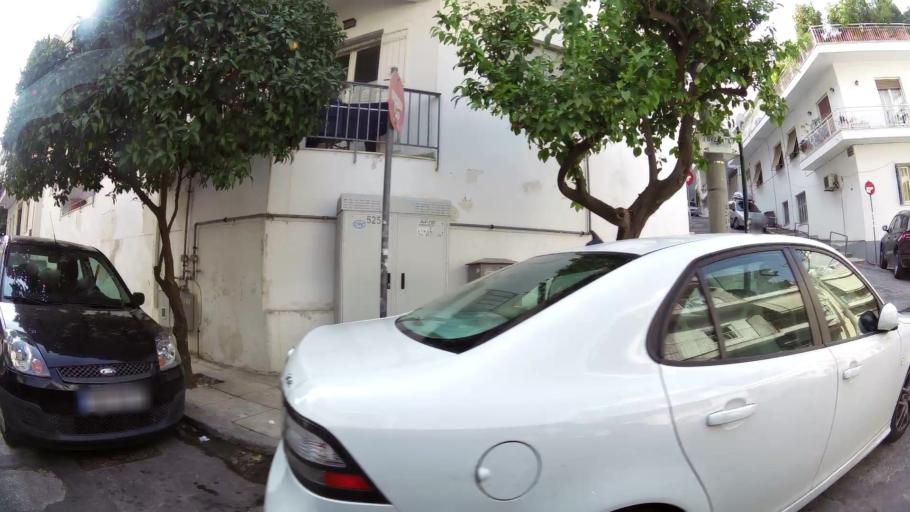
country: GR
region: Attica
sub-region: Nomarchia Athinas
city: Galatsi
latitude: 38.0111
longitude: 23.7554
